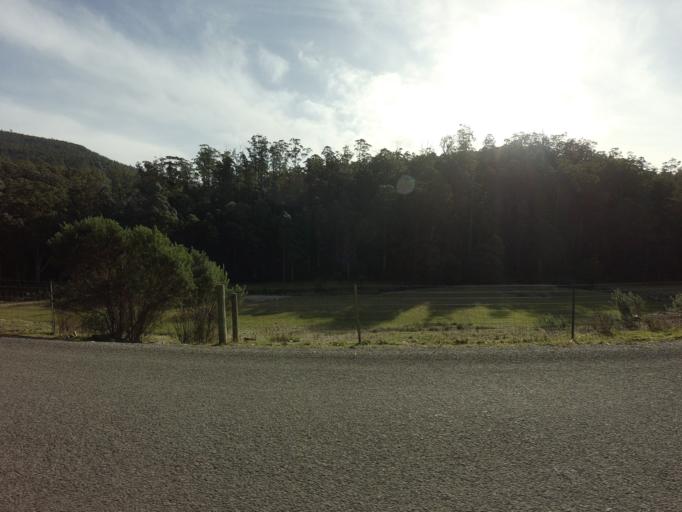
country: AU
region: Tasmania
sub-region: Huon Valley
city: Huonville
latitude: -43.0438
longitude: 147.1216
